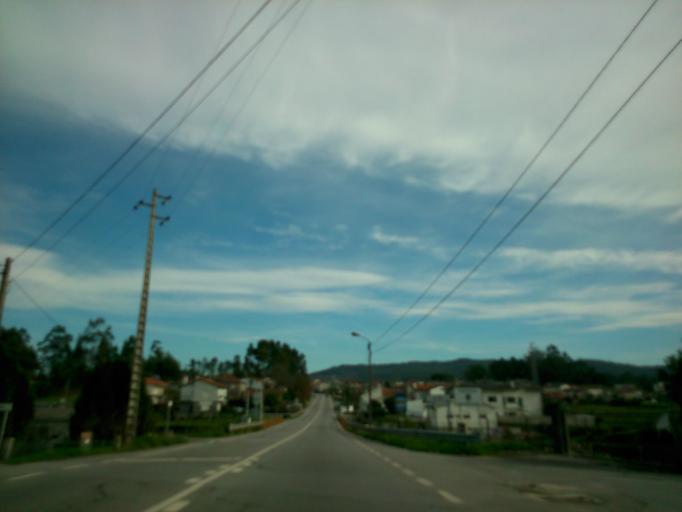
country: PT
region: Braga
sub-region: Barcelos
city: Barcelos
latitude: 41.5195
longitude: -8.5859
